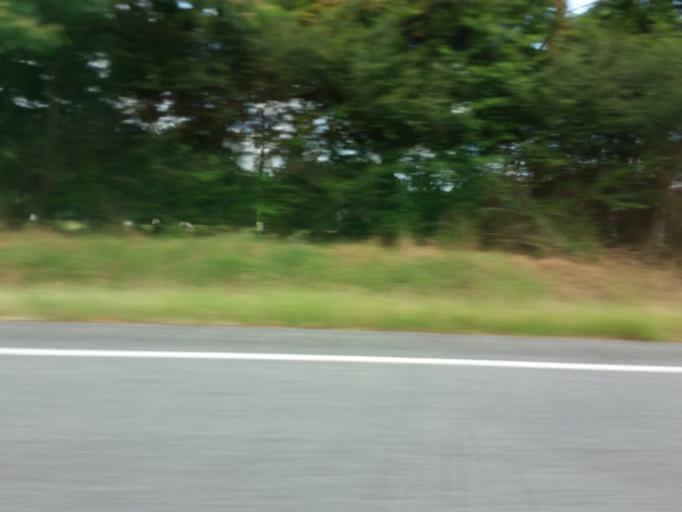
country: US
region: Alabama
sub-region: Sumter County
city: York
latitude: 32.3897
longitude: -88.2000
